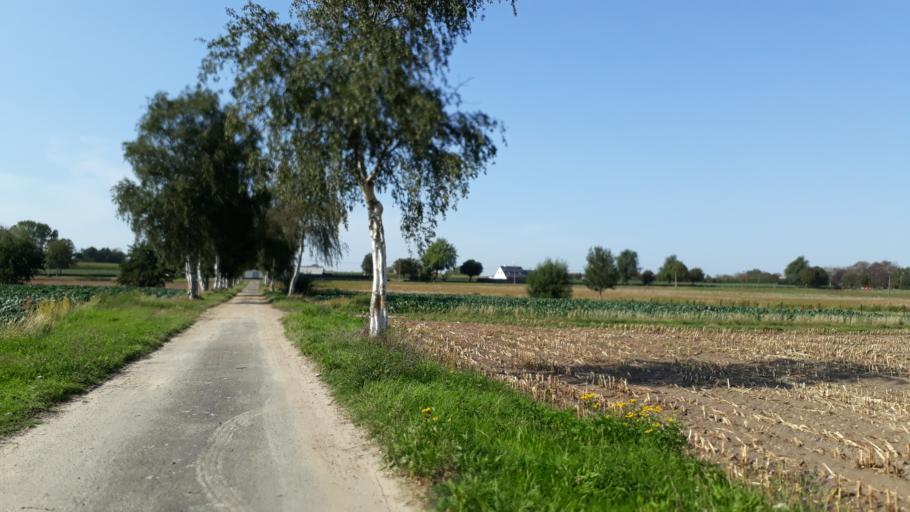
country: BE
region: Flanders
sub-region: Provincie West-Vlaanderen
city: Torhout
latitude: 51.0898
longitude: 3.1267
